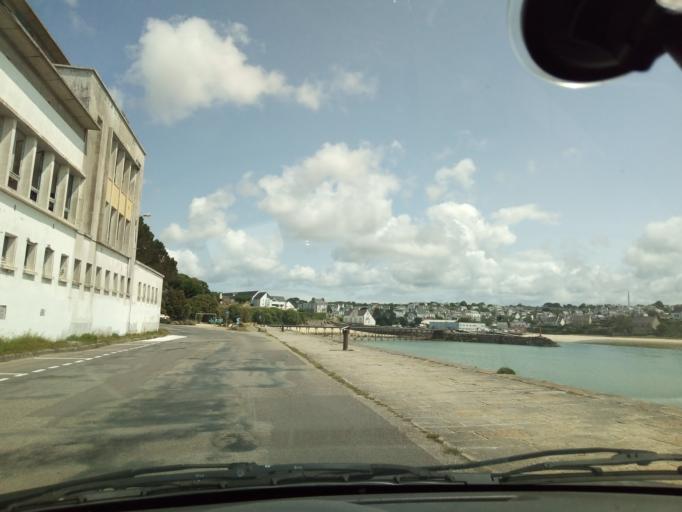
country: FR
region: Brittany
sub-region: Departement du Finistere
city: Audierne
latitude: 48.0154
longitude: -4.5387
